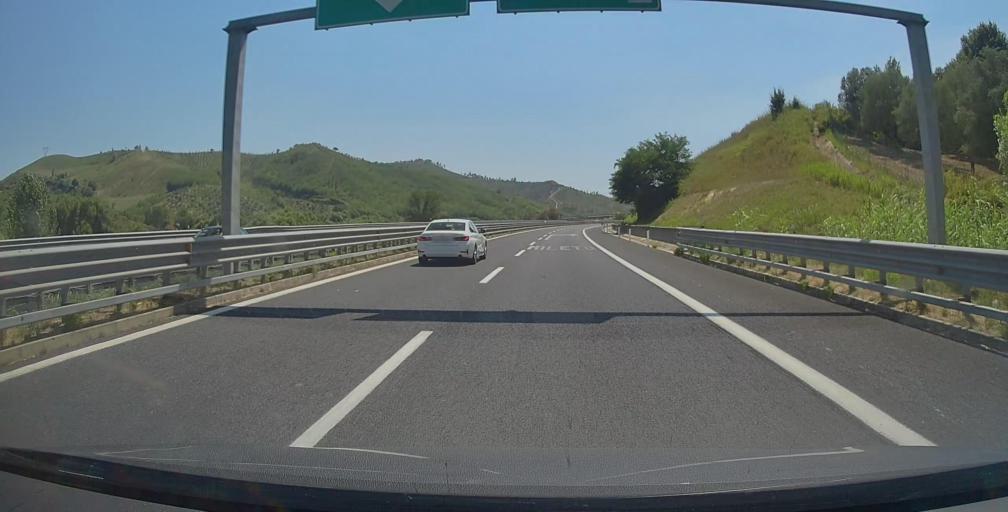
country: IT
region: Calabria
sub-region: Provincia di Vibo-Valentia
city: Paravati
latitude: 38.5681
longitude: 16.0871
